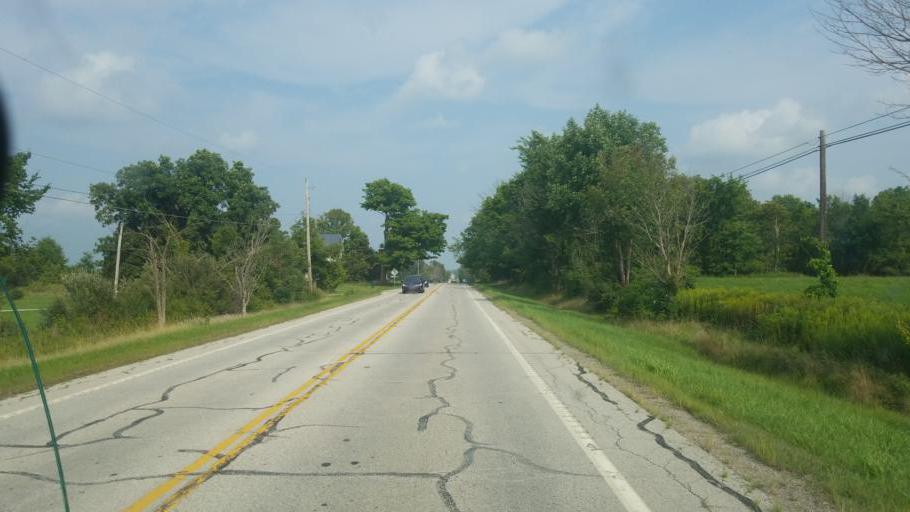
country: US
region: Ohio
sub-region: Medina County
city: Medina
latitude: 41.1676
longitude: -81.9730
